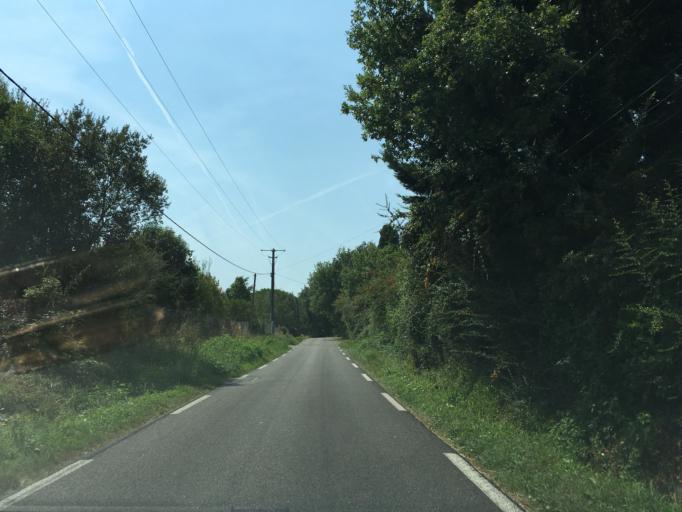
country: FR
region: Midi-Pyrenees
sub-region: Departement du Tarn-et-Garonne
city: Saint-Nauphary
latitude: 43.9677
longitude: 1.3939
